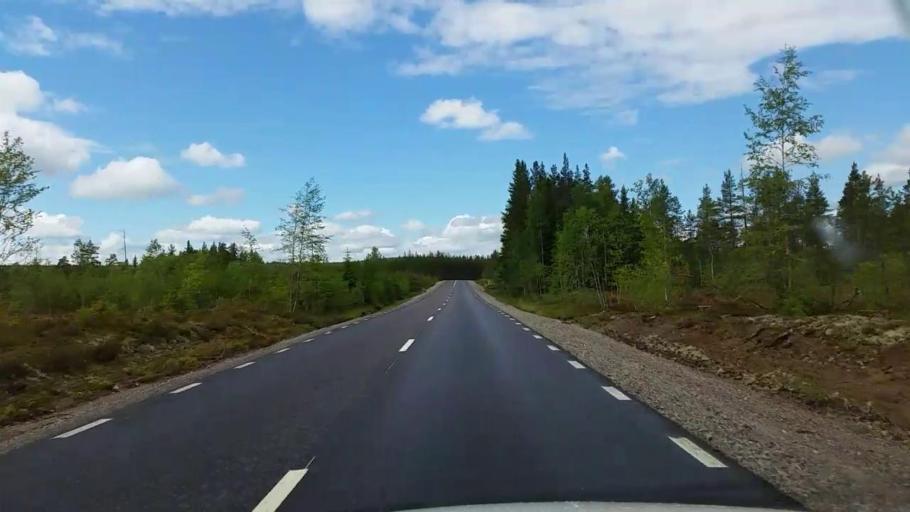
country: SE
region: Gaevleborg
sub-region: Sandvikens Kommun
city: Jarbo
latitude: 60.8783
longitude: 16.3924
